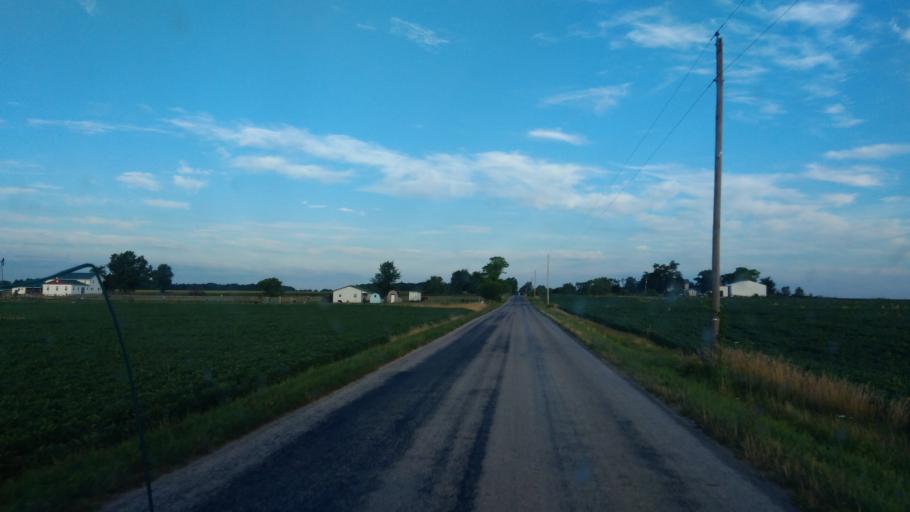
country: US
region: Indiana
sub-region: Adams County
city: Geneva
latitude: 40.6053
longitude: -85.0320
